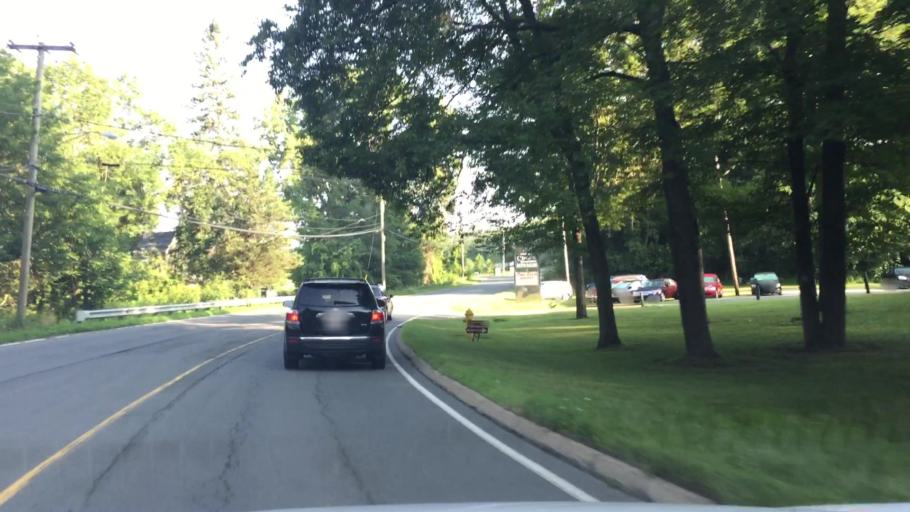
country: US
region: Massachusetts
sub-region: Berkshire County
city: Dalton
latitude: 42.4647
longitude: -73.1923
